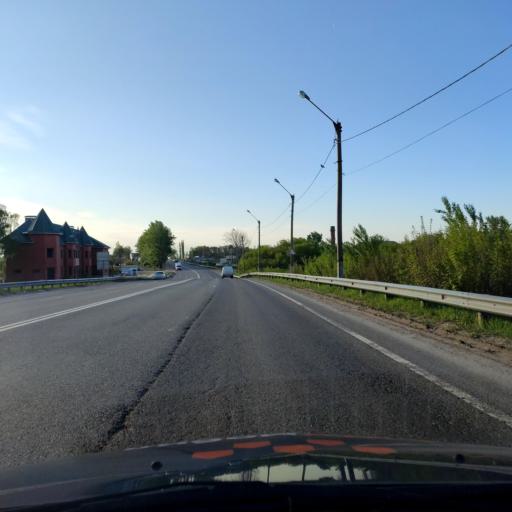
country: RU
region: Lipetsk
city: Yelets
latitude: 52.5972
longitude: 38.4768
